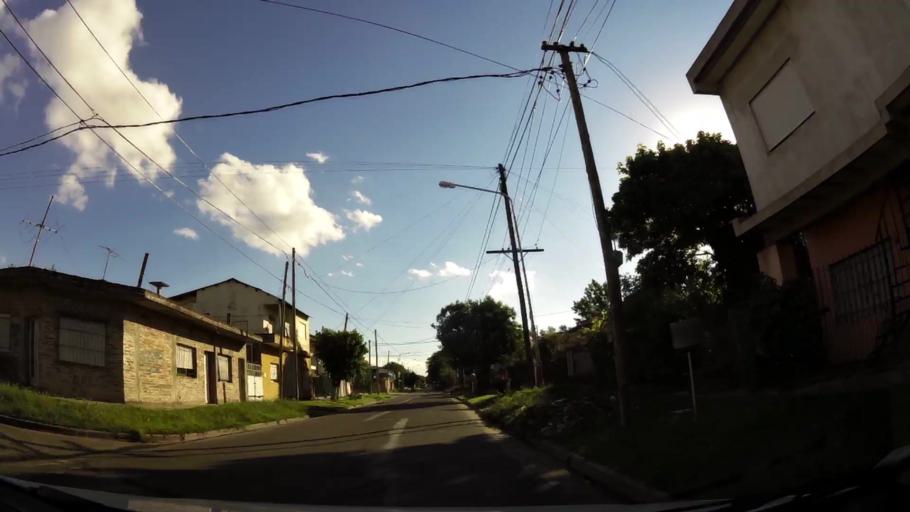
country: AR
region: Buenos Aires
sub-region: Partido de Moron
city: Moron
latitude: -34.6785
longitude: -58.6198
